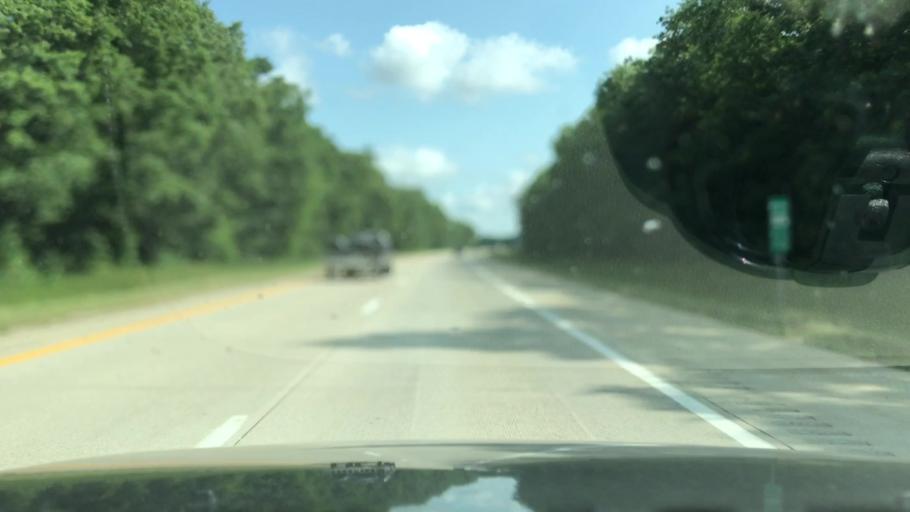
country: US
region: Michigan
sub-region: Montcalm County
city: Howard City
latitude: 43.4122
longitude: -85.5053
